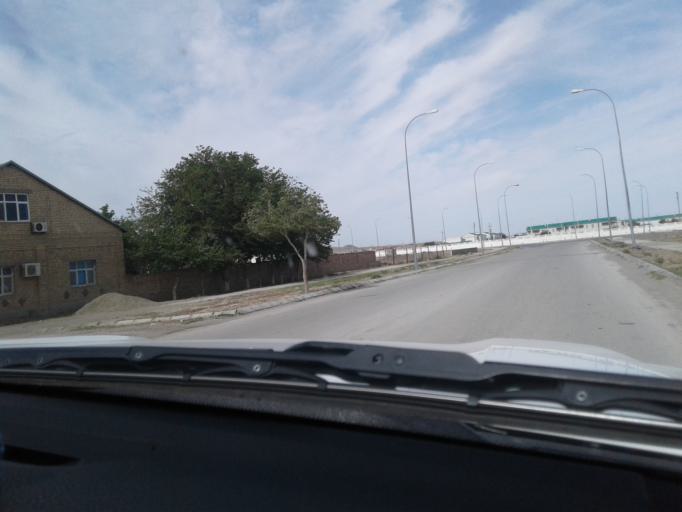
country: TM
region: Balkan
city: Gazanjyk
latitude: 39.2452
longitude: 55.5008
